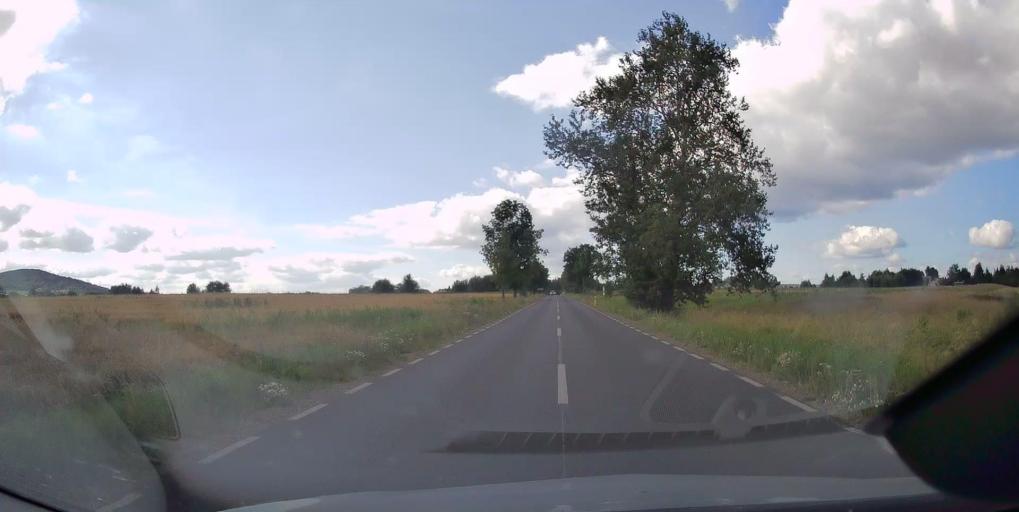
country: PL
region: Swietokrzyskie
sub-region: Powiat kielecki
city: Bodzentyn
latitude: 50.9272
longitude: 20.9826
